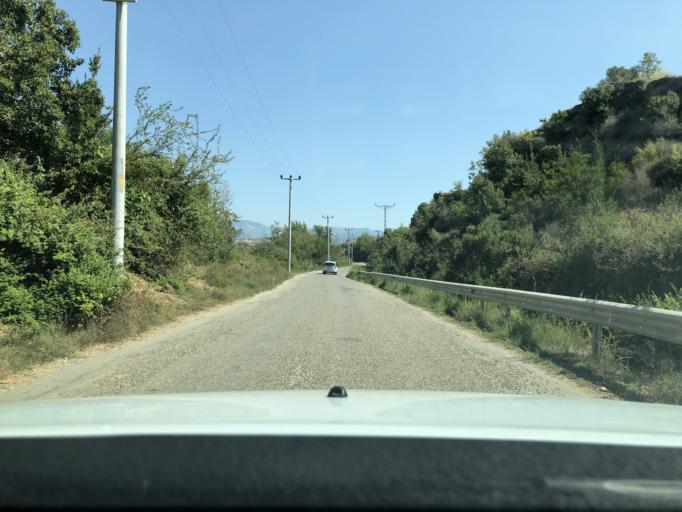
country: TR
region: Antalya
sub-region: Manavgat
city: Manavgat
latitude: 36.7994
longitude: 31.4675
